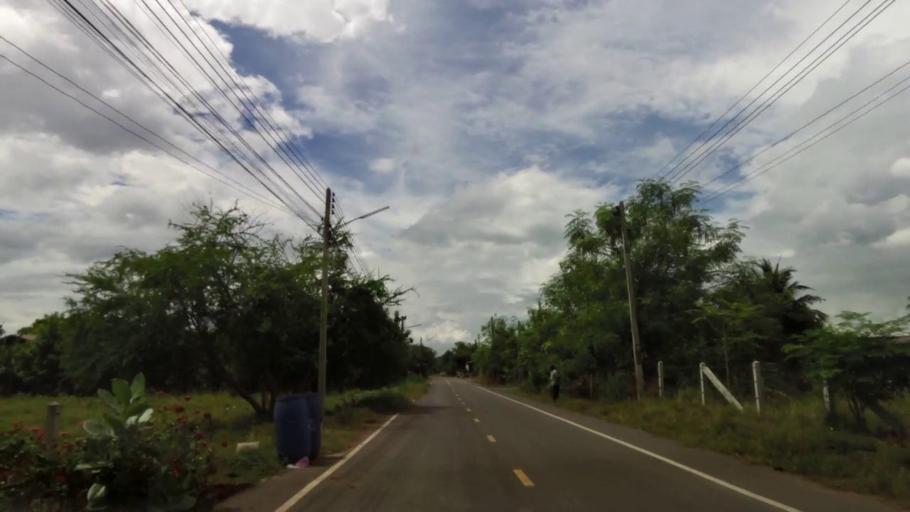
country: TH
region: Nakhon Sawan
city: Phai Sali
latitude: 15.6024
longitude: 100.6508
